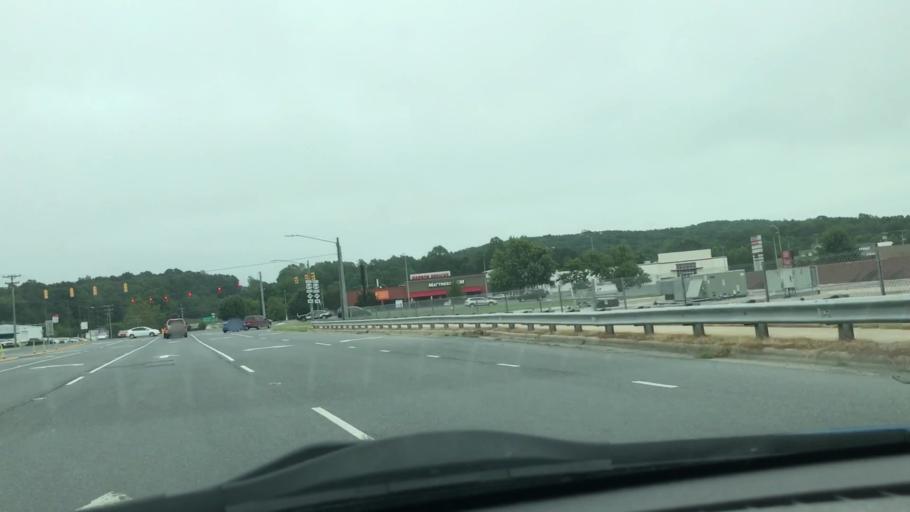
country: US
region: North Carolina
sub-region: Randolph County
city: Asheboro
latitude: 35.6989
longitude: -79.7887
